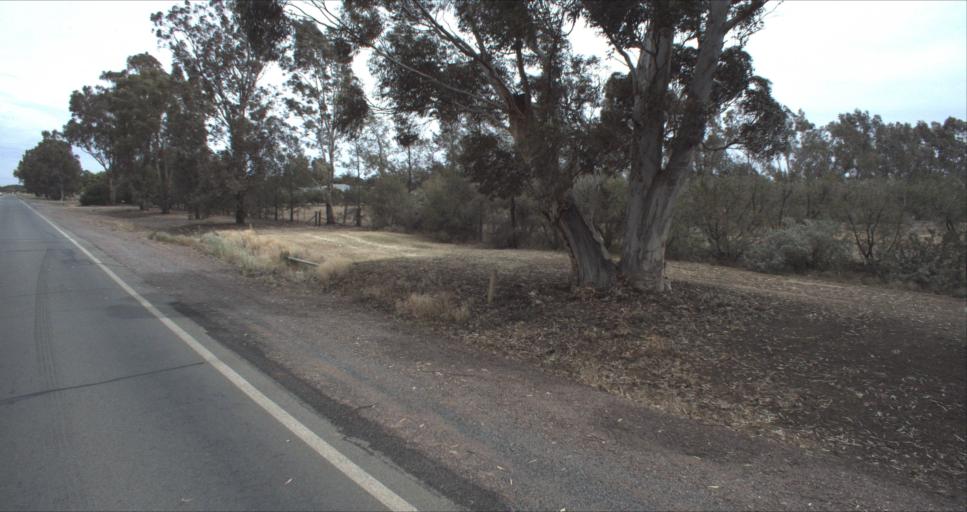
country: AU
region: New South Wales
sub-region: Leeton
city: Leeton
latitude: -34.5240
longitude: 146.4123
